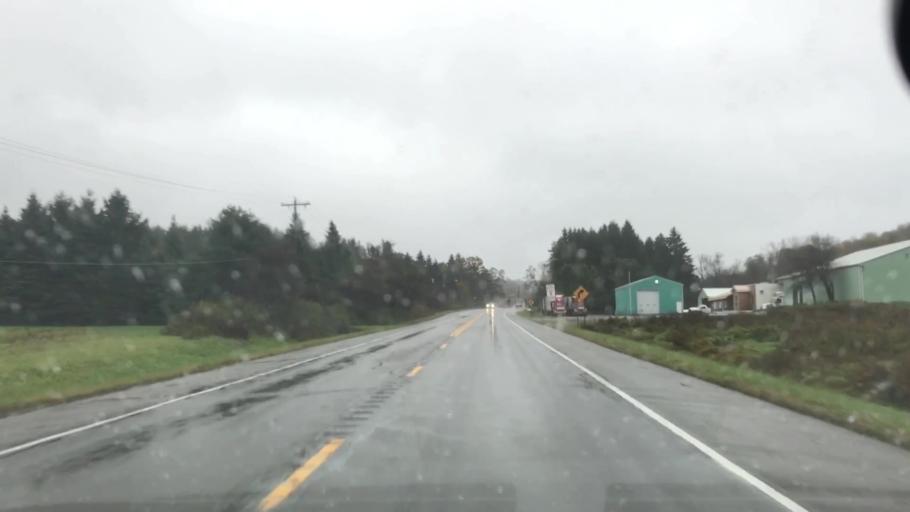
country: US
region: New York
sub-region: Erie County
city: Springville
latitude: 42.3993
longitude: -78.6795
